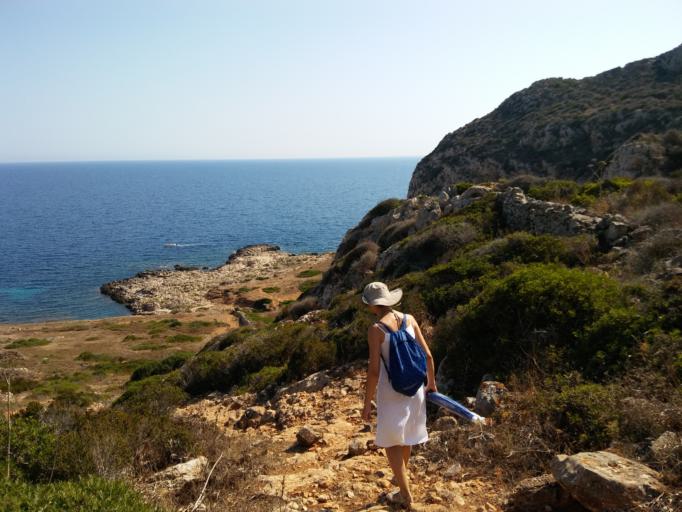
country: IT
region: Sicily
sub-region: Trapani
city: Favignana
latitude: 37.9973
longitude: 12.3454
